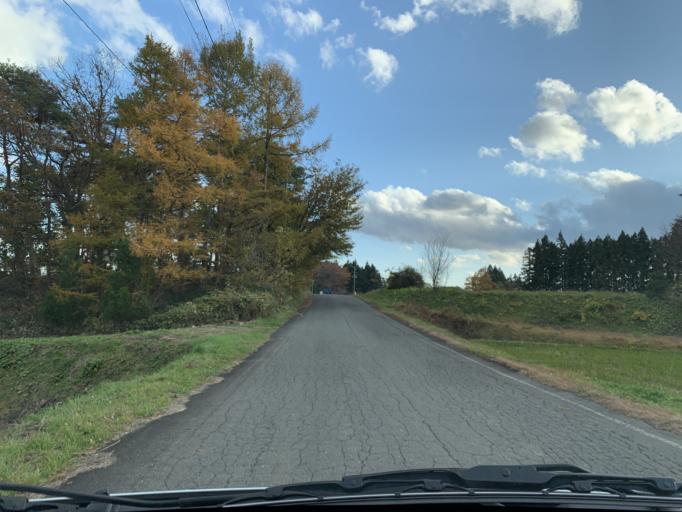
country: JP
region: Iwate
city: Mizusawa
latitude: 39.1114
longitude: 141.0009
